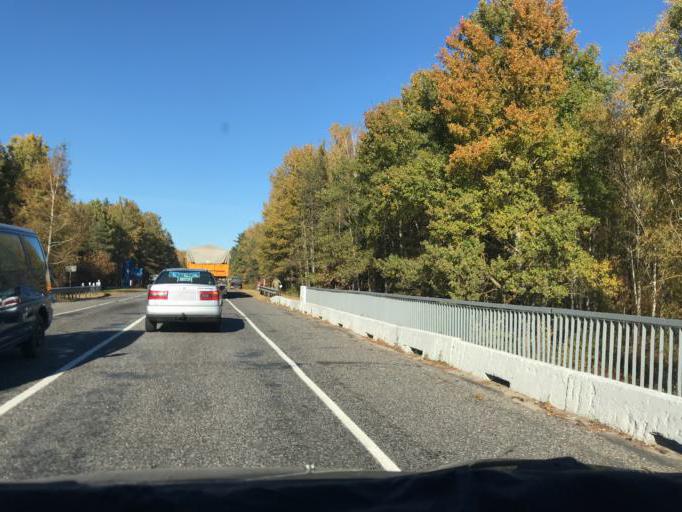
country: BY
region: Gomel
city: Yel'sk
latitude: 51.8536
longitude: 29.2250
